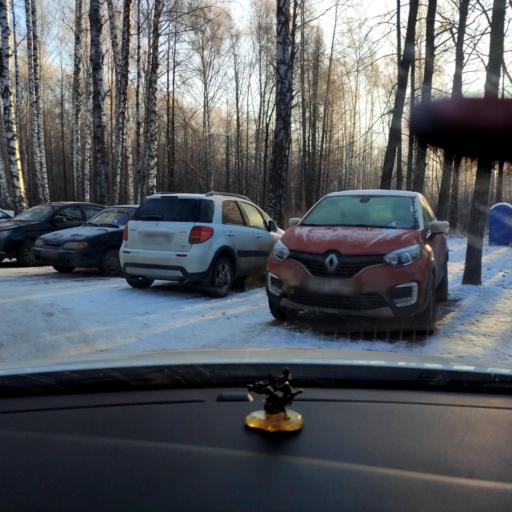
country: RU
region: Tatarstan
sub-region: Gorod Kazan'
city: Kazan
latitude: 55.6765
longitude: 49.0984
